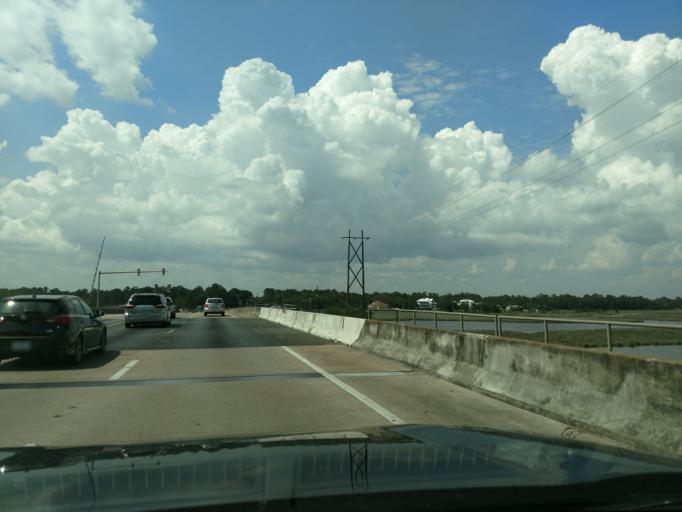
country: US
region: Mississippi
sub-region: Jackson County
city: Ocean Springs
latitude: 30.4192
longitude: -88.8277
